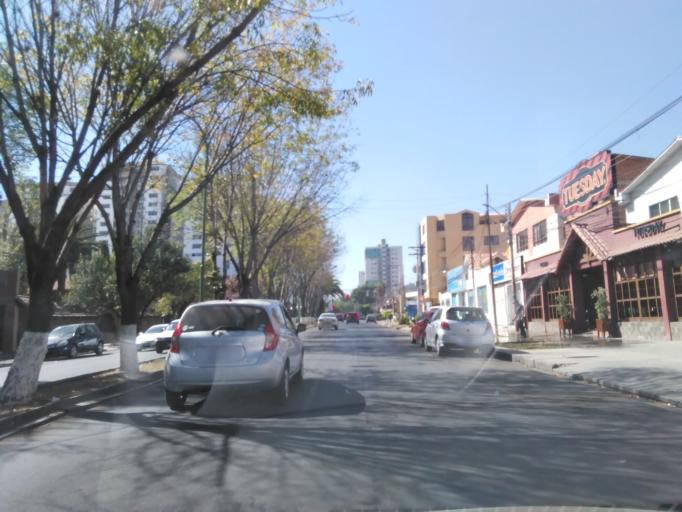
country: BO
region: Cochabamba
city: Cochabamba
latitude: -17.3732
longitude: -66.1525
